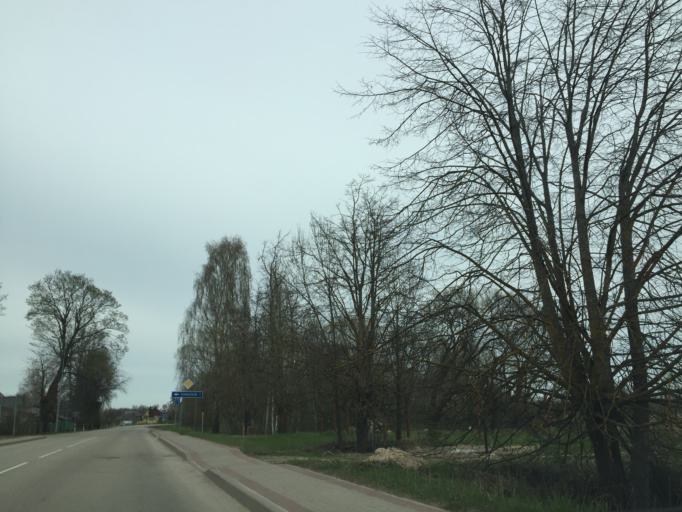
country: LV
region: Ludzas Rajons
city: Ludza
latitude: 56.5636
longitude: 27.7245
